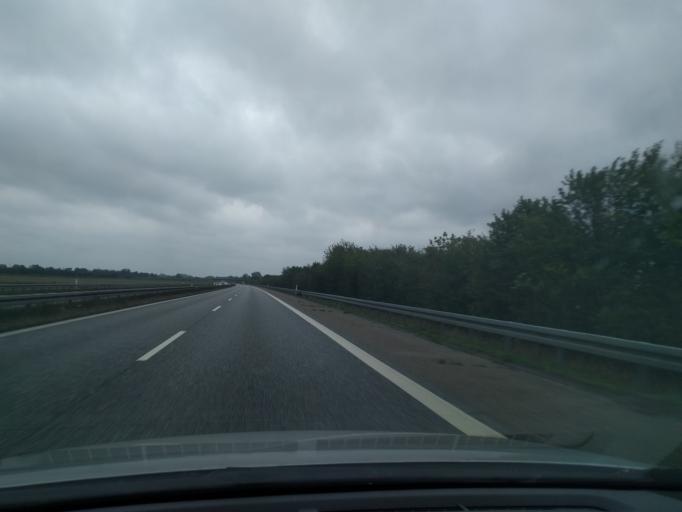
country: DK
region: Zealand
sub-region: Soro Kommune
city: Frederiksberg
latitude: 55.4486
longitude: 11.6710
